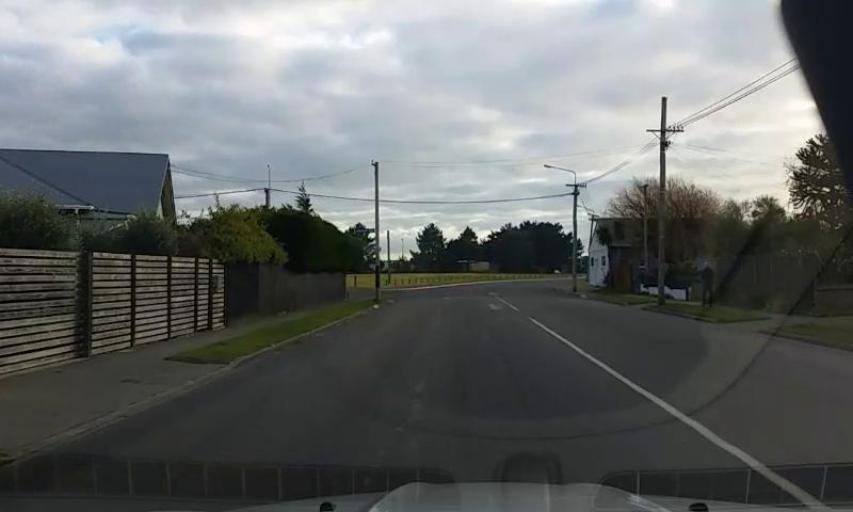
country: NZ
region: Canterbury
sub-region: Christchurch City
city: Christchurch
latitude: -43.5152
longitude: 172.7292
